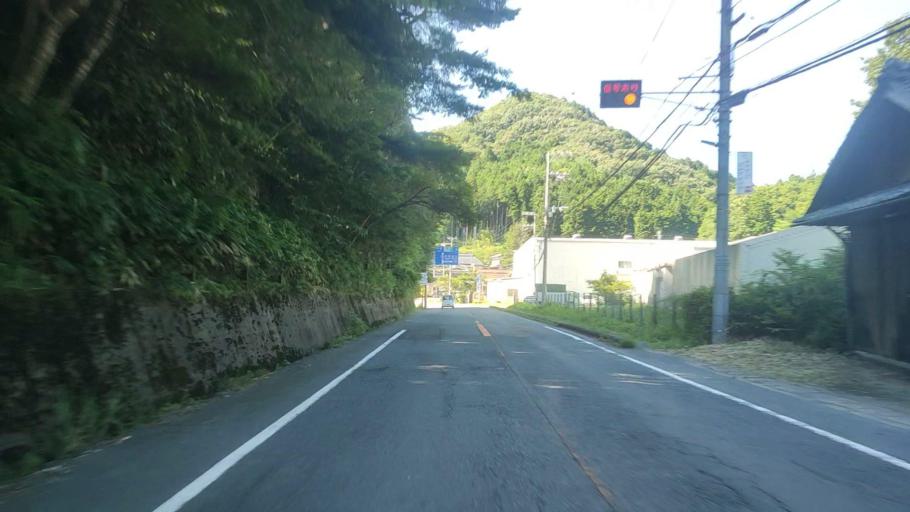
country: JP
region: Nara
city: Haibara-akanedai
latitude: 34.5839
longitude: 135.9693
